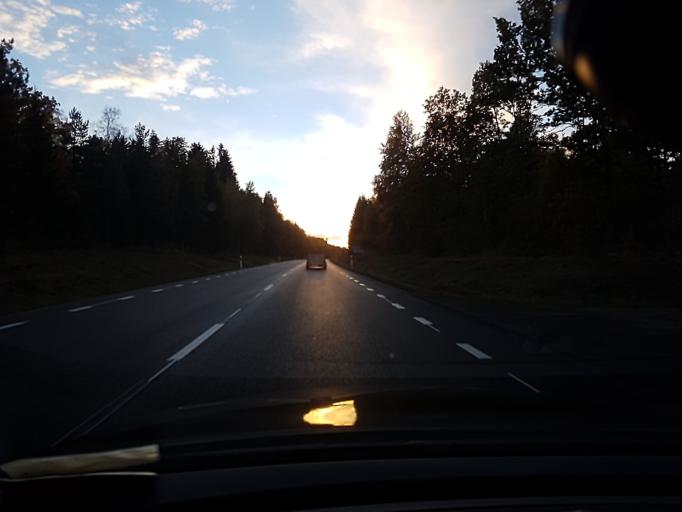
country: SE
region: Kronoberg
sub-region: Ljungby Kommun
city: Ljungby
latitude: 56.7575
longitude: 13.7601
